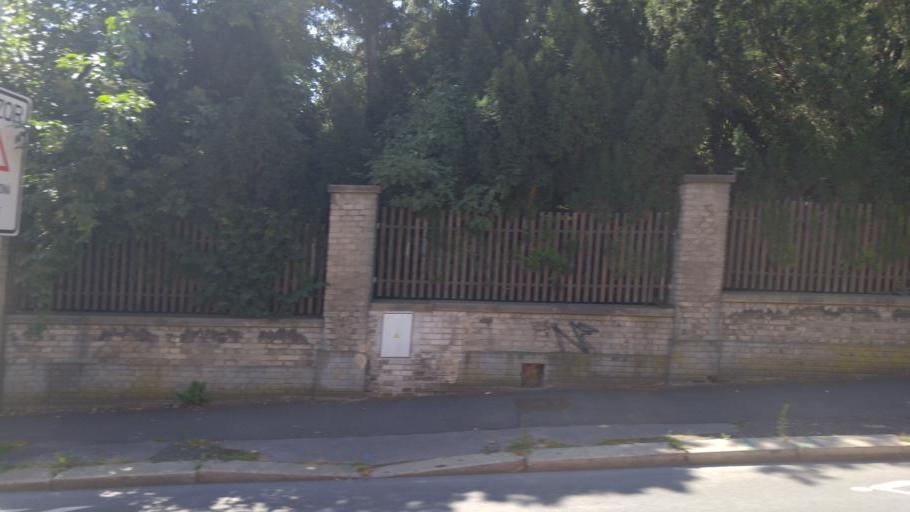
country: CZ
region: Praha
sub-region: Praha 1
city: Mala Strana
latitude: 50.0928
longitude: 14.3814
